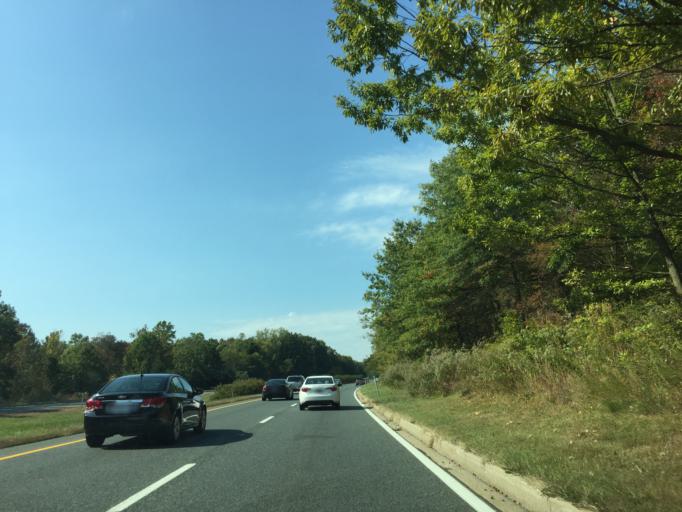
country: US
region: Maryland
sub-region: Baltimore County
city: Perry Hall
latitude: 39.3806
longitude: -76.4814
